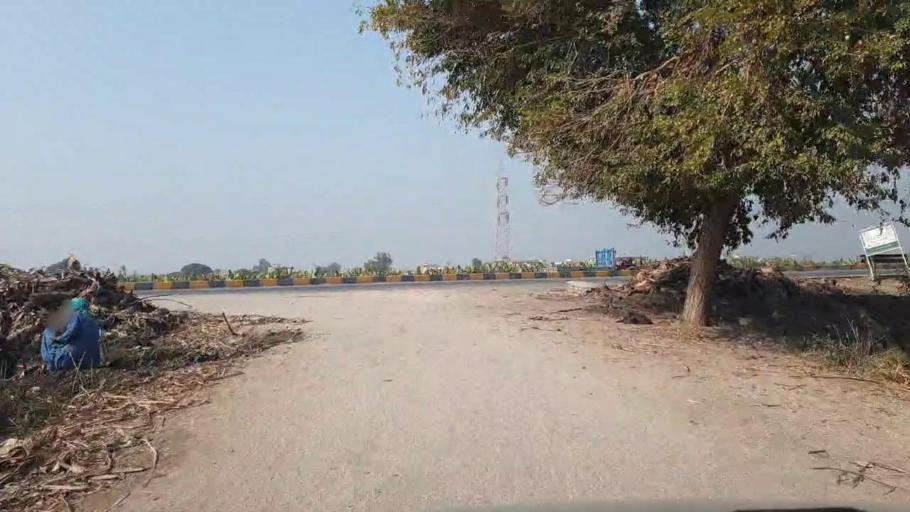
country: PK
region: Sindh
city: Sakrand
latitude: 25.9917
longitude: 68.3621
